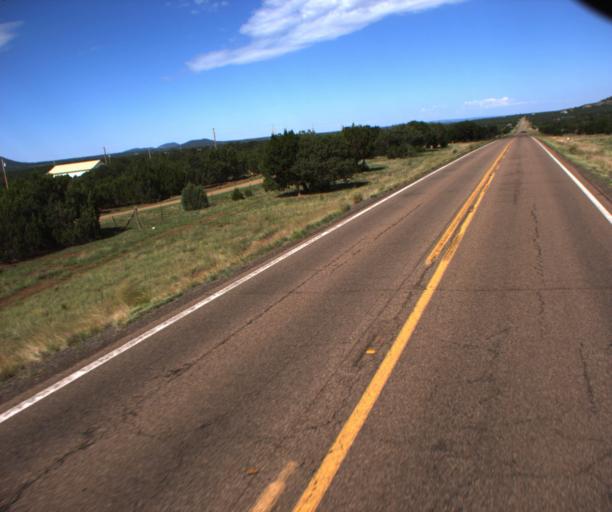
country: US
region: Arizona
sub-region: Navajo County
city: Pinetop-Lakeside
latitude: 34.2734
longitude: -109.7611
